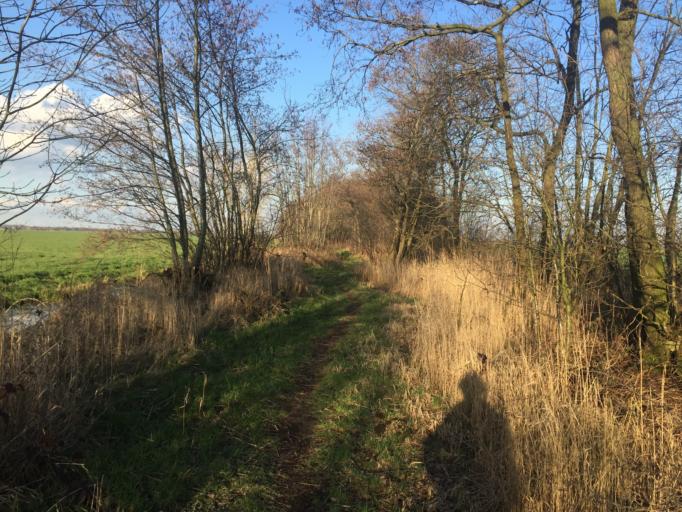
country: NL
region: Utrecht
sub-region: Gemeente Oudewater
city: Oudewater
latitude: 52.0374
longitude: 4.8178
